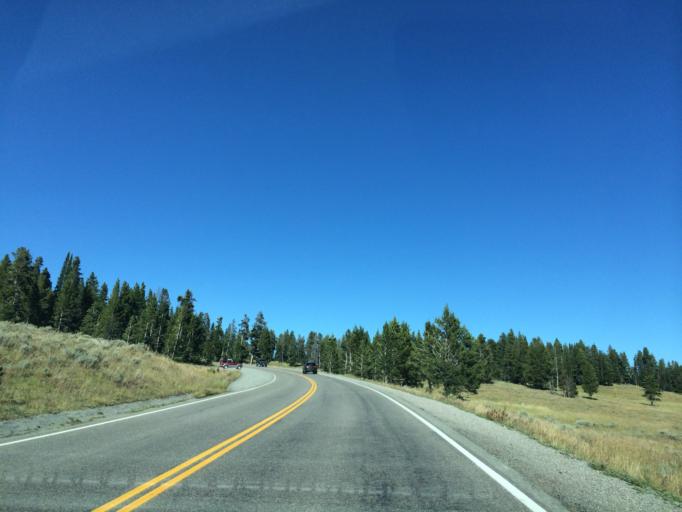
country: US
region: Montana
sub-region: Gallatin County
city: West Yellowstone
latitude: 44.7222
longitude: -110.4949
